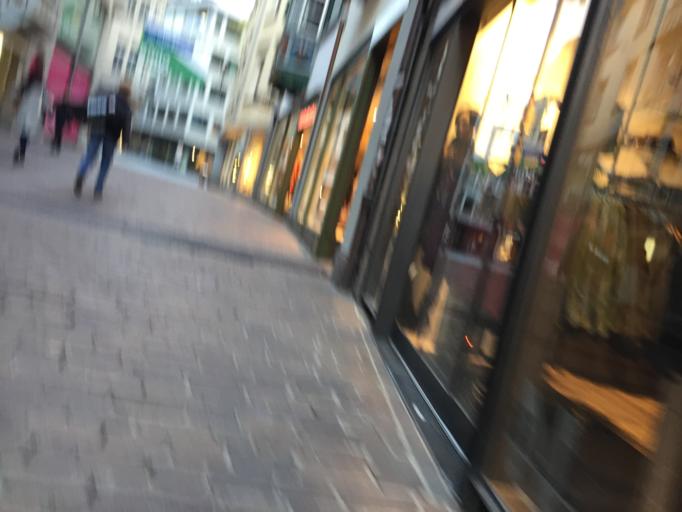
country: CH
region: Saint Gallen
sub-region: Wahlkreis St. Gallen
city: Sankt Gallen
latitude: 47.4249
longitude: 9.3772
